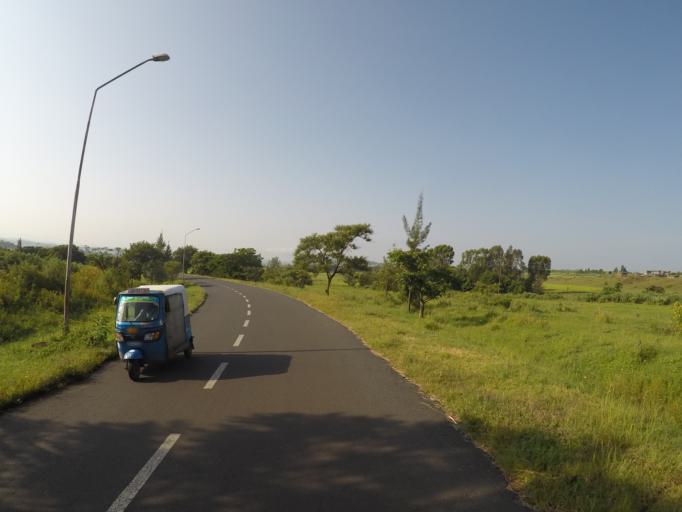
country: ET
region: Amhara
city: Gondar
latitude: 12.5190
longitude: 37.4295
